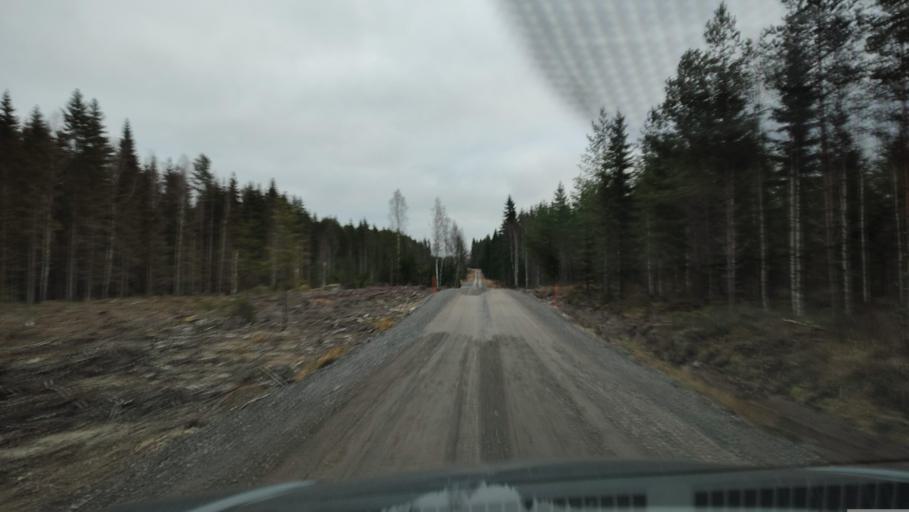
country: FI
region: Southern Ostrobothnia
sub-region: Suupohja
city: Karijoki
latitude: 62.2044
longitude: 21.5957
